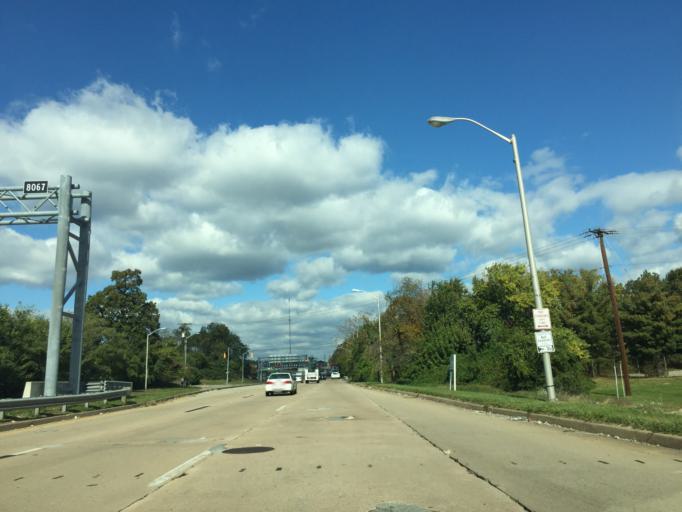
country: US
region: Maryland
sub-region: Baltimore County
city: Rosedale
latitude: 39.3128
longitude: -76.5433
